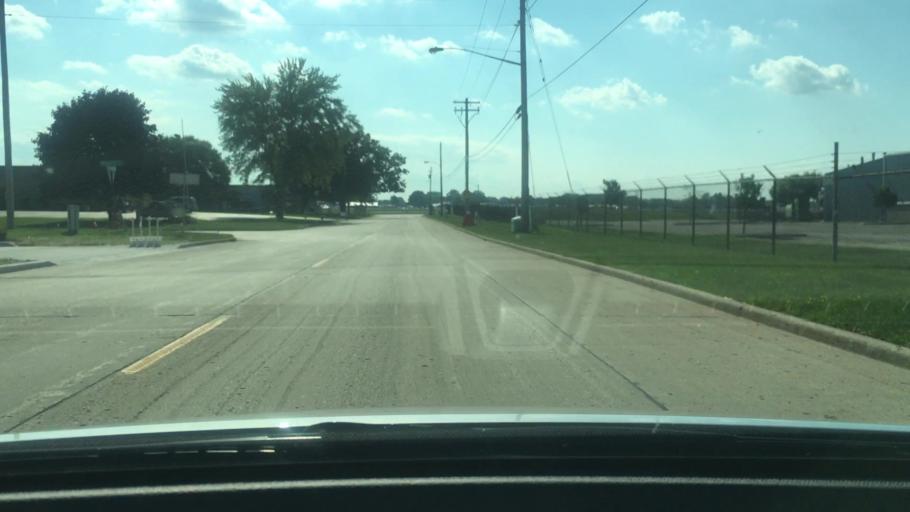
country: US
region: Wisconsin
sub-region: Winnebago County
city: Oshkosh
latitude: 43.9813
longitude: -88.5499
